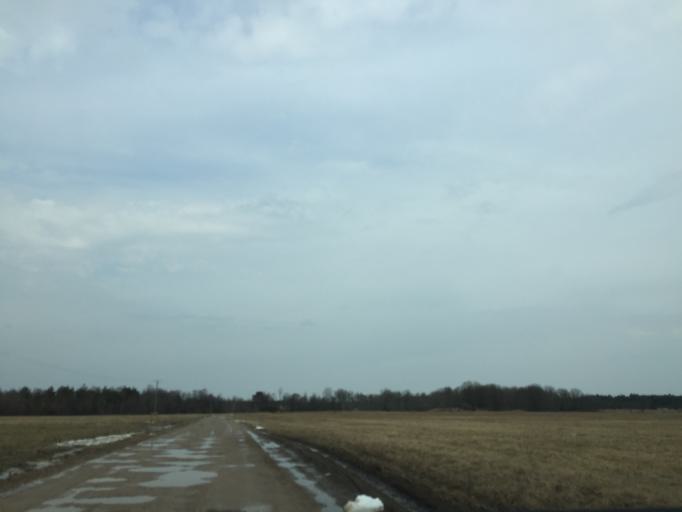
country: EE
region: Saare
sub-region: Kuressaare linn
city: Kuressaare
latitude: 58.4354
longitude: 22.1435
